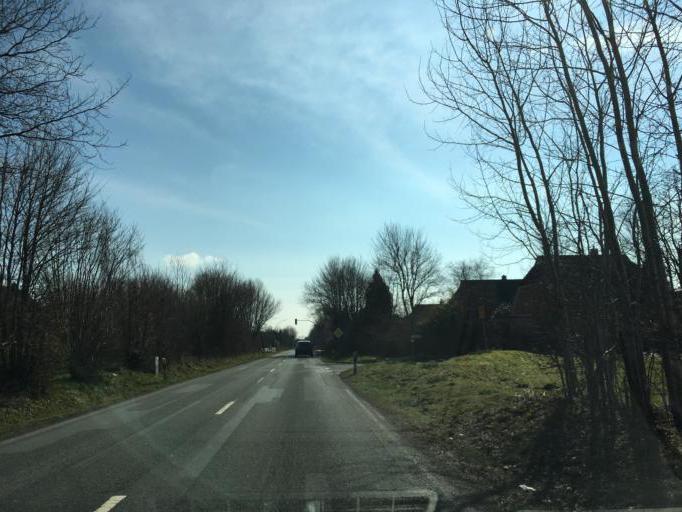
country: DE
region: Schleswig-Holstein
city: Escheburg
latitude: 53.4707
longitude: 10.3107
